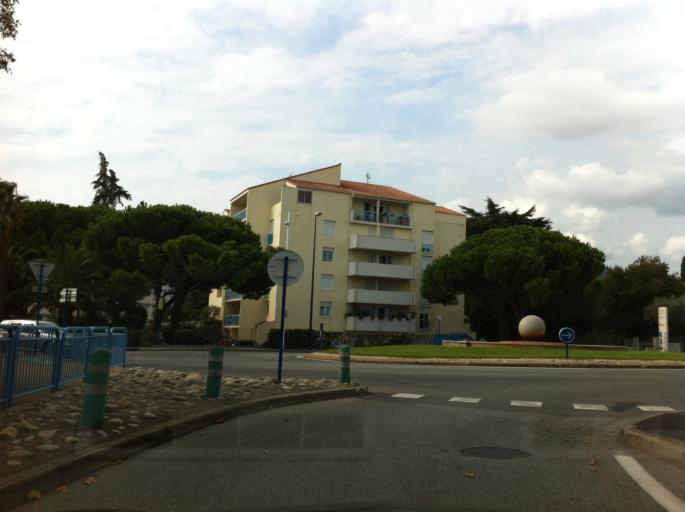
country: FR
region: Provence-Alpes-Cote d'Azur
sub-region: Departement du Var
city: Sainte-Maxime
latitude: 43.3144
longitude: 6.6316
